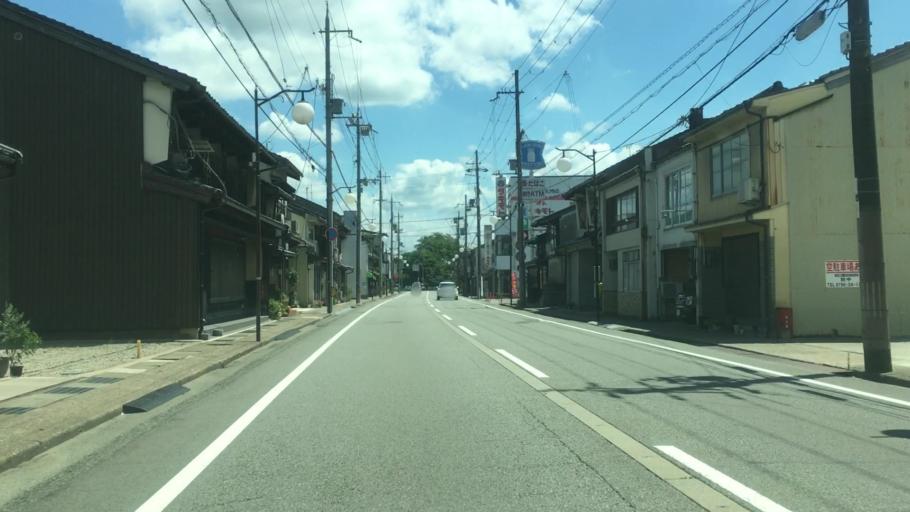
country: JP
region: Hyogo
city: Toyooka
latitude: 35.5371
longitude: 134.8251
